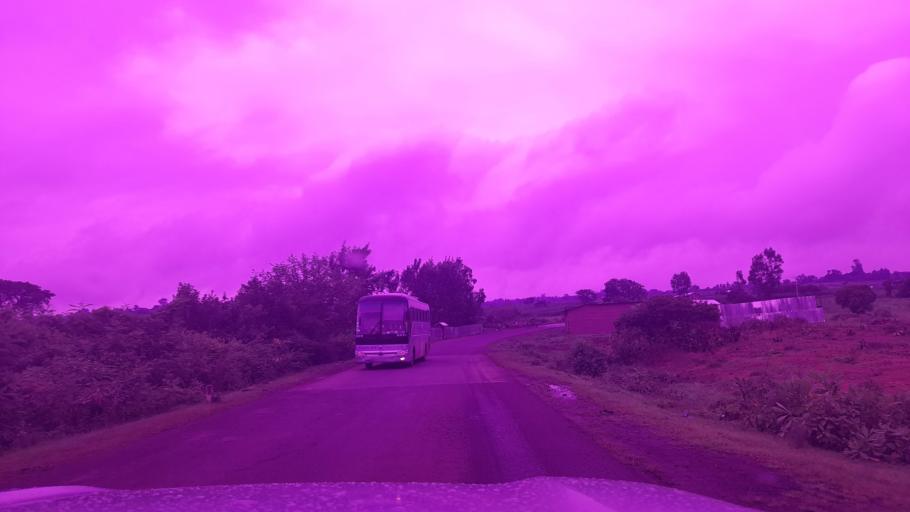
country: ET
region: Oromiya
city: Jima
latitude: 7.6883
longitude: 37.2323
